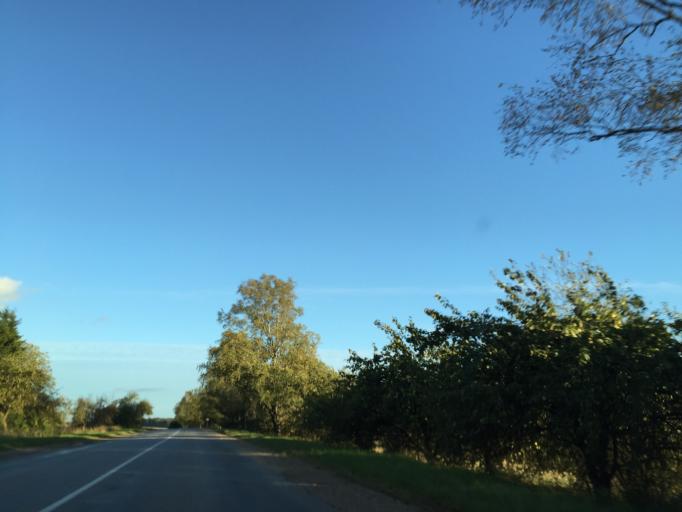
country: LV
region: Saldus Rajons
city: Saldus
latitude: 56.7200
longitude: 22.3877
